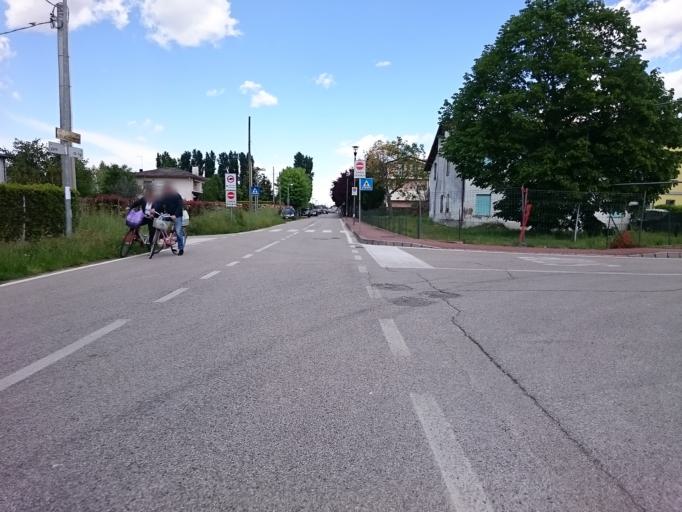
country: IT
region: Veneto
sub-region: Provincia di Padova
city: Terradura
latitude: 45.3460
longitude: 11.8168
